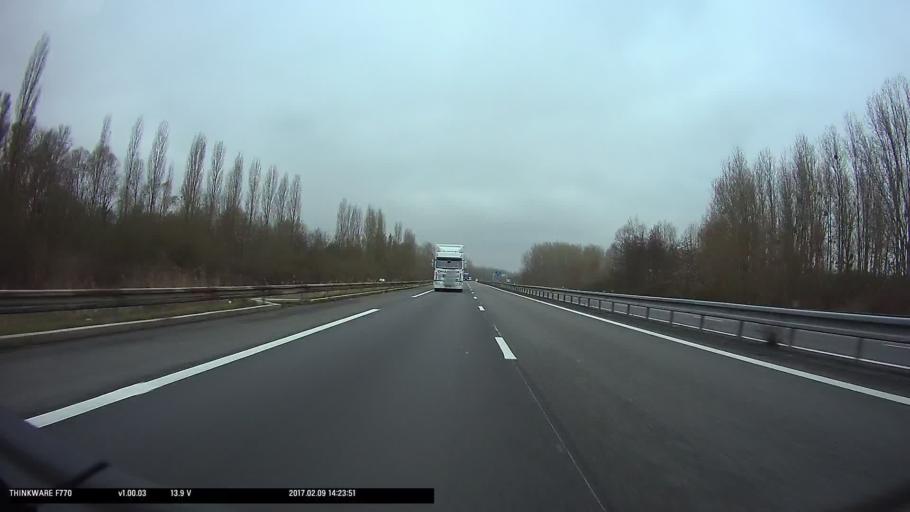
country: FR
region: Centre
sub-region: Departement du Cher
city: Foecy
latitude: 47.2031
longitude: 2.1297
